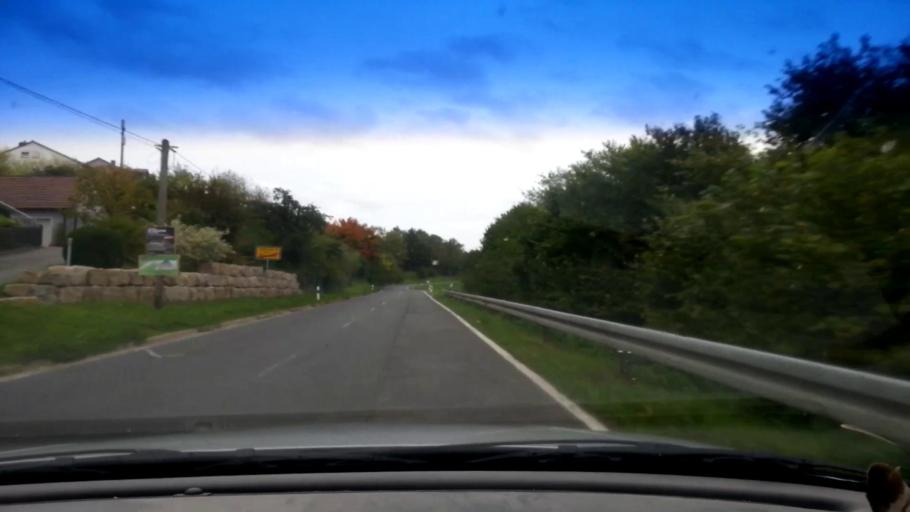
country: DE
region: Bavaria
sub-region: Upper Franconia
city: Lauter
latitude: 49.9665
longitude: 10.8016
